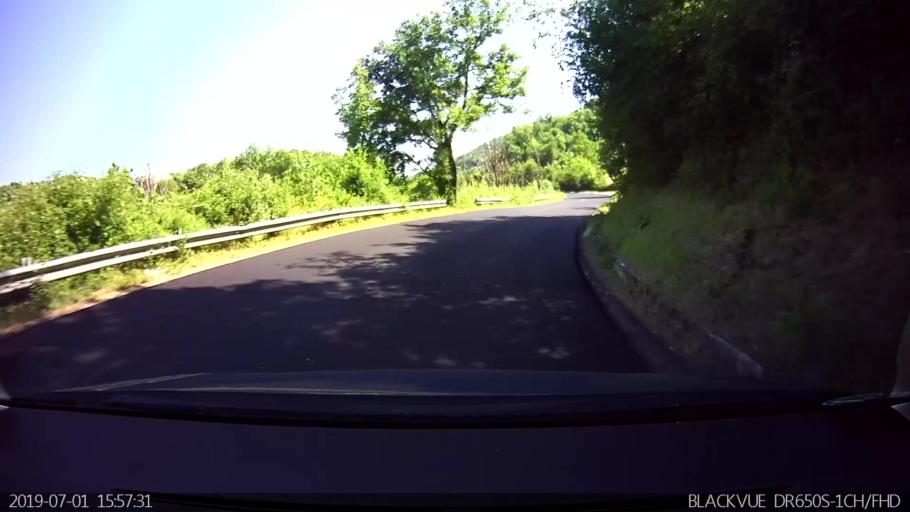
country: IT
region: Latium
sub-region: Provincia di Frosinone
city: Sant'Angelo in Villa-Giglio
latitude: 41.6755
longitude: 13.4220
